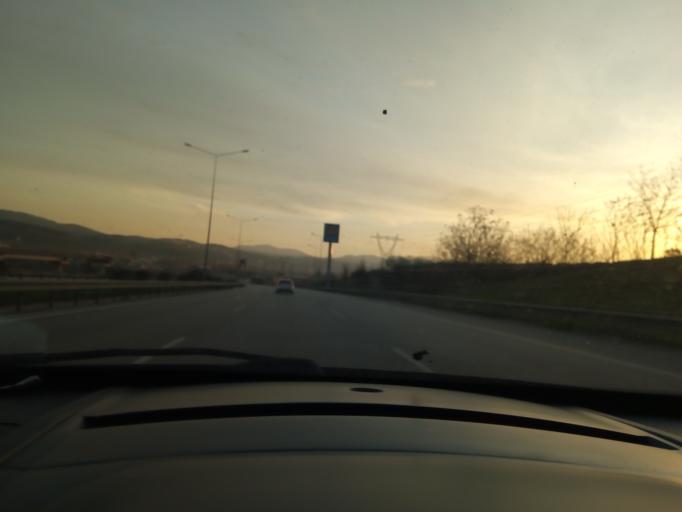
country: TR
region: Bursa
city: Niluefer
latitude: 40.2788
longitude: 28.9883
